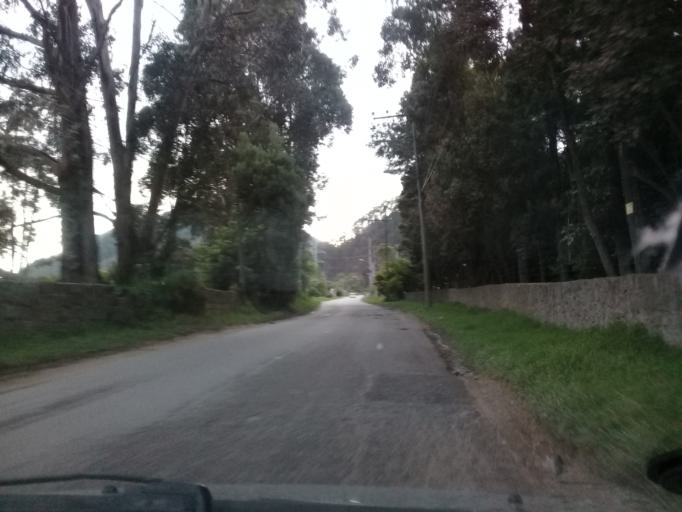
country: CO
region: Cundinamarca
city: Cajica
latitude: 4.9277
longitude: -74.0577
